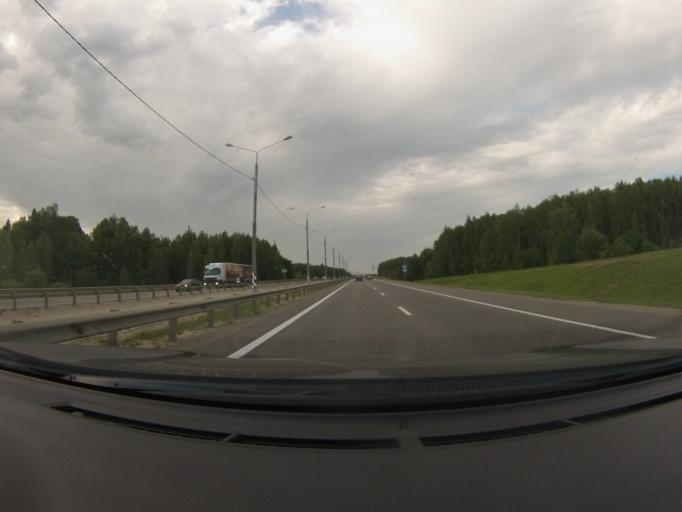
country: RU
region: Tula
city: Zaokskiy
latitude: 54.6814
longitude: 37.5067
